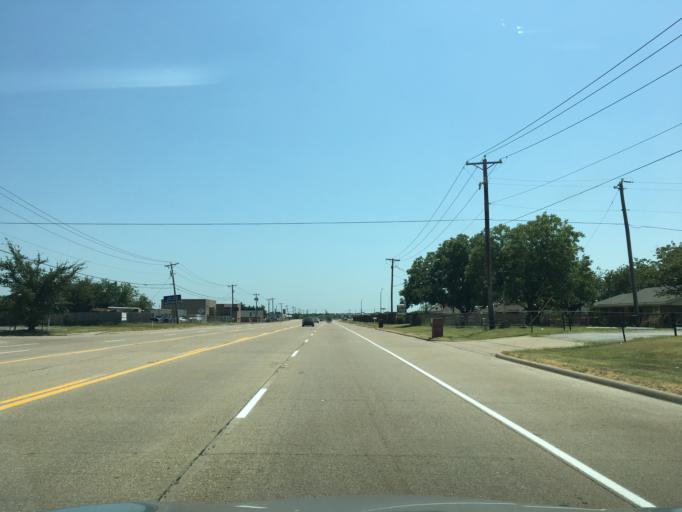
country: US
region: Texas
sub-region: Tarrant County
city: Edgecliff Village
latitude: 32.6210
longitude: -97.3487
